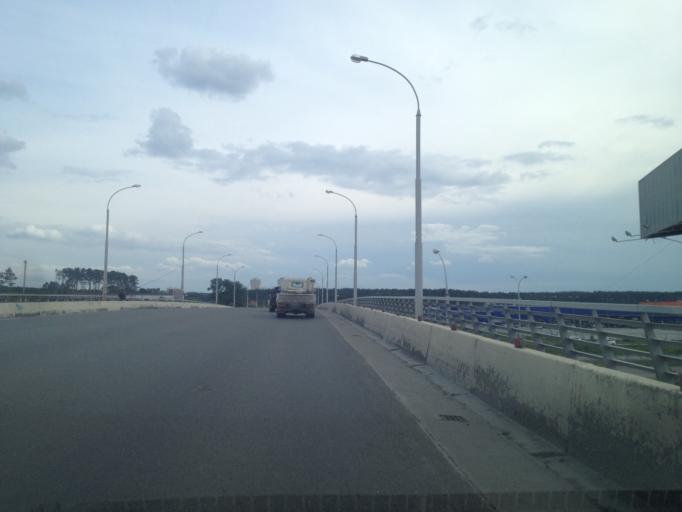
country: RU
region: Sverdlovsk
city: Shirokaya Rechka
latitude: 56.8274
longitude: 60.5135
